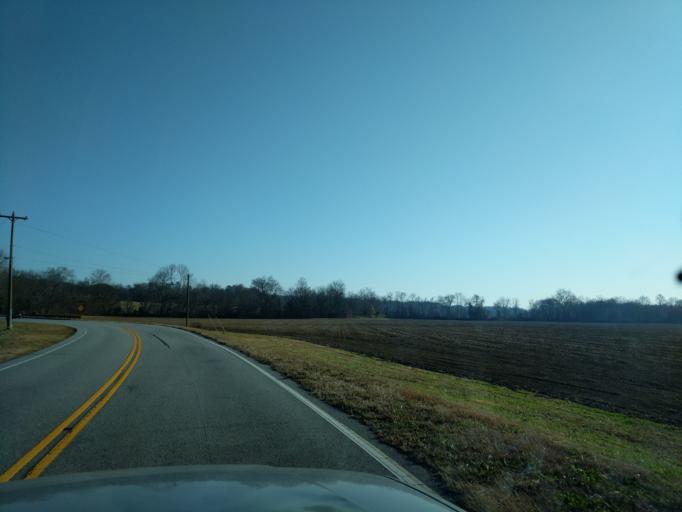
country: US
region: South Carolina
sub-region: Spartanburg County
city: Landrum
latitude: 35.1871
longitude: -82.1472
